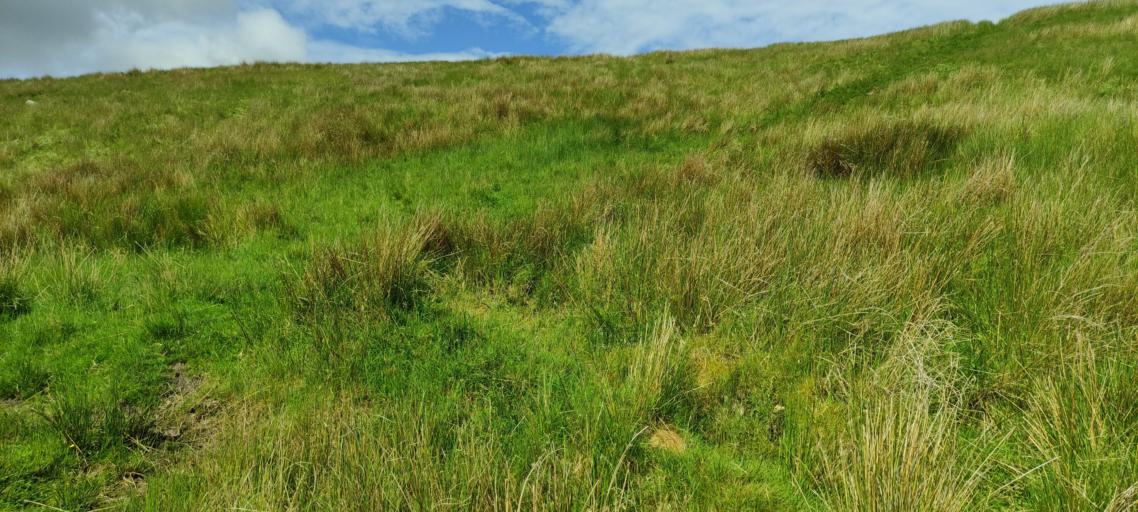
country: GB
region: England
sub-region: Cumbria
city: Kirkby Stephen
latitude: 54.3740
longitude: -2.3523
